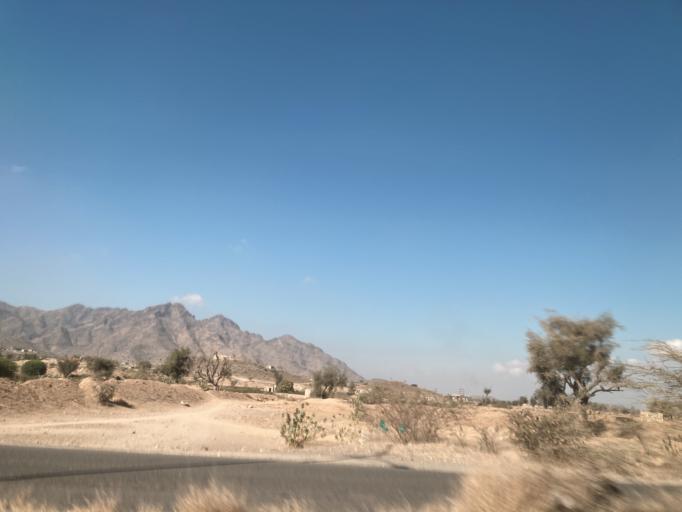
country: YE
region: Ad Dali'
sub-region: Al Hussein
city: Al Husayn
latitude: 13.8043
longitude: 44.7256
